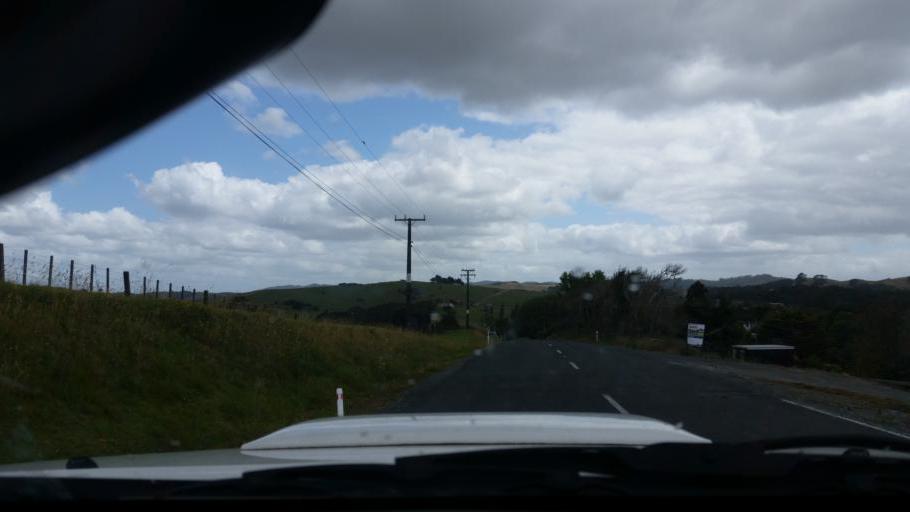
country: NZ
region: Northland
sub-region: Whangarei
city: Ruakaka
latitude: -36.1018
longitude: 174.3509
